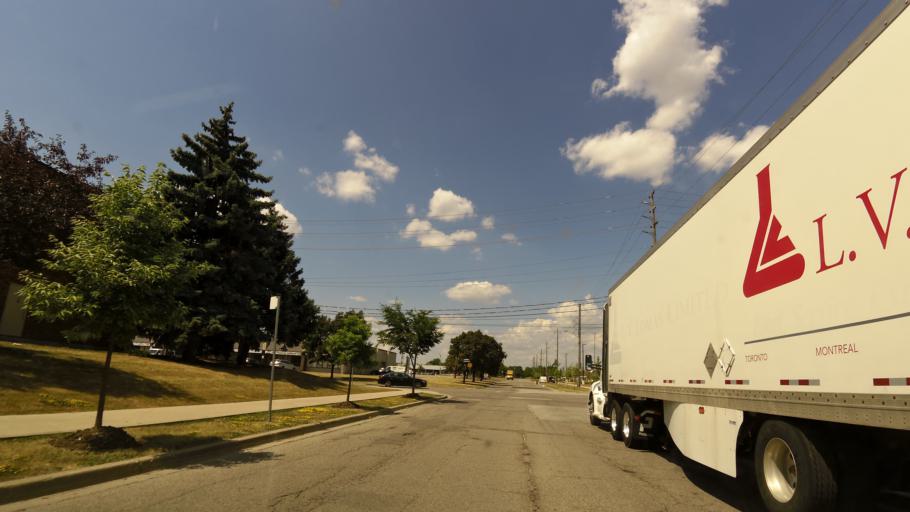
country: CA
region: Ontario
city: Etobicoke
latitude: 43.7382
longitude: -79.6074
